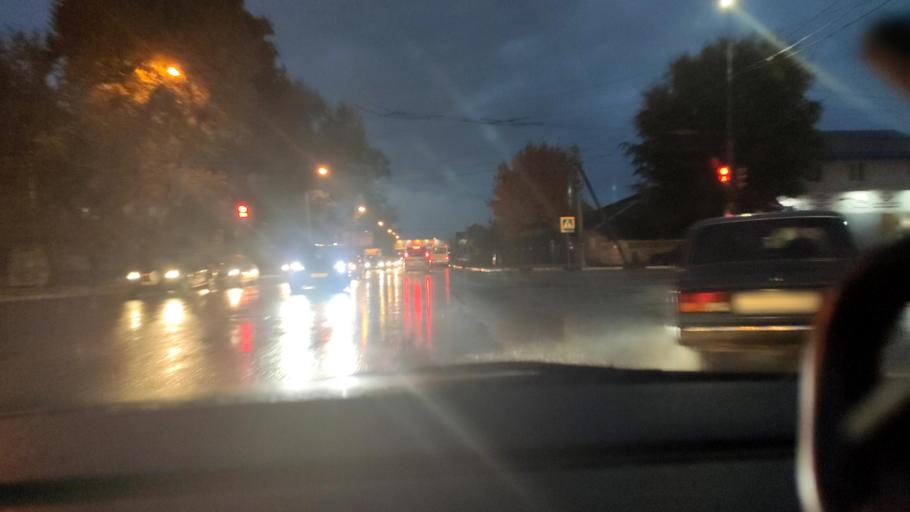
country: RU
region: Voronezj
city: Voronezh
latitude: 51.6990
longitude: 39.1964
